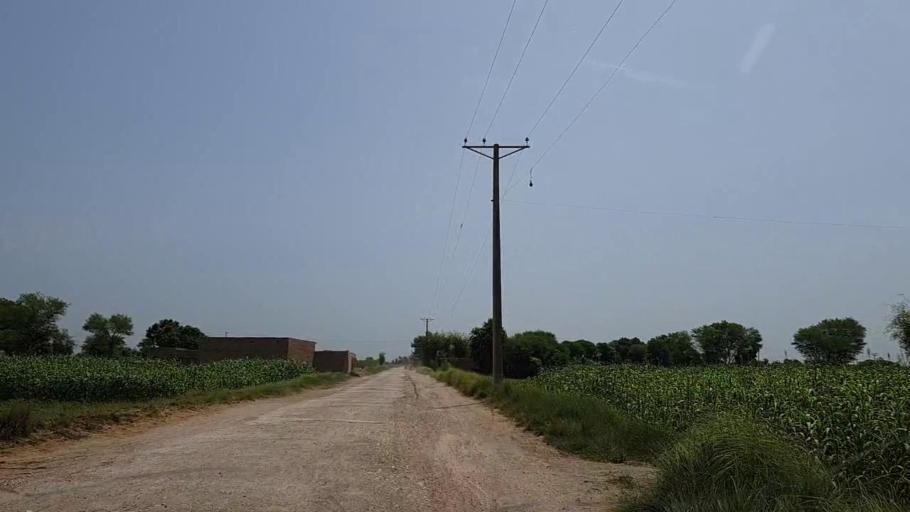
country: PK
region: Sindh
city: Naushahro Firoz
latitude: 26.8427
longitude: 67.9871
